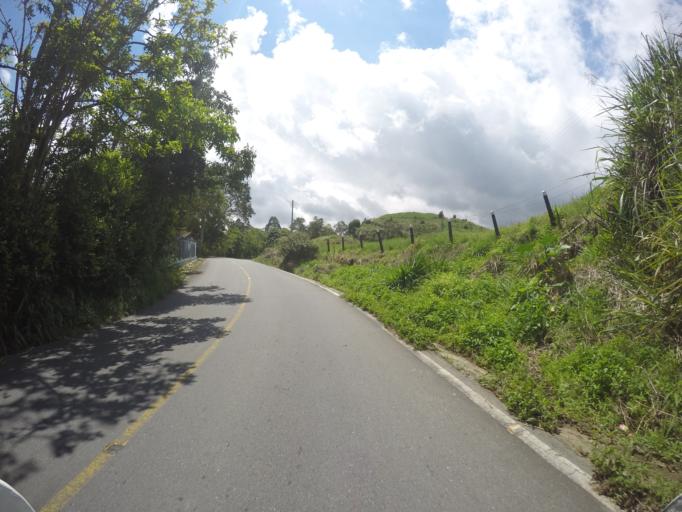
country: CO
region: Quindio
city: Filandia
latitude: 4.6468
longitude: -75.6801
